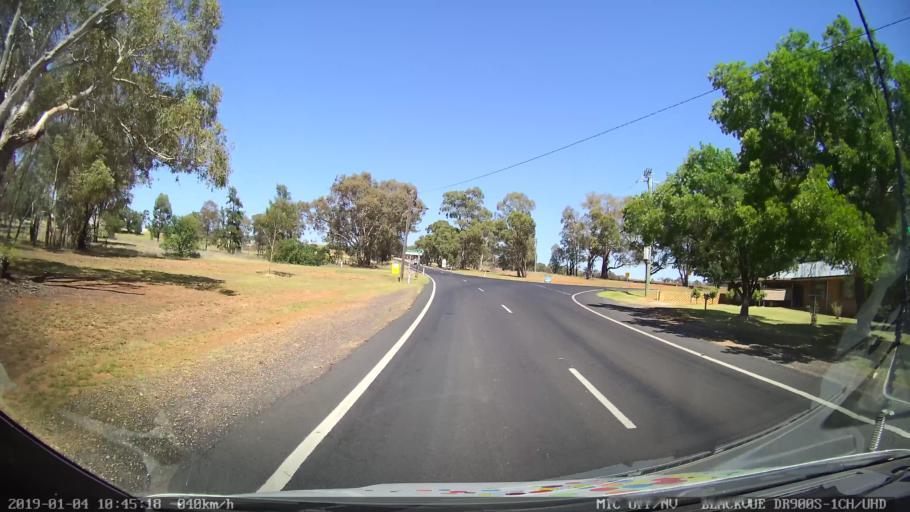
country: AU
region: New South Wales
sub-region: Cabonne
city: Molong
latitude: -33.2895
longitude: 148.7277
